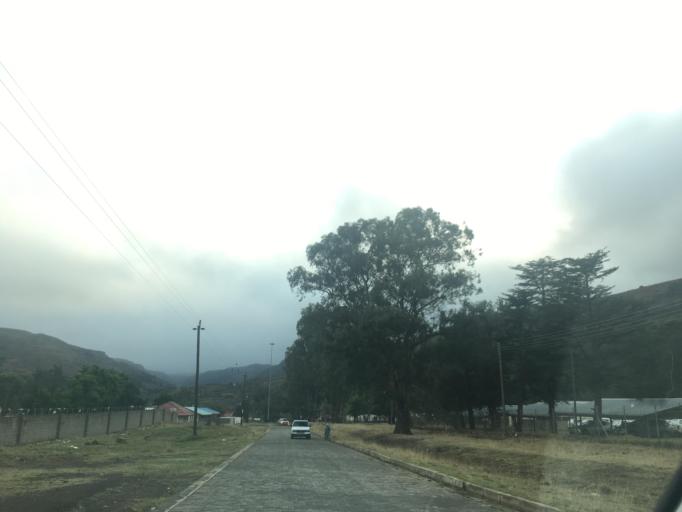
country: ZA
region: Eastern Cape
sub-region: Chris Hani District Municipality
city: Cala
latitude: -31.5242
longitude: 27.6986
